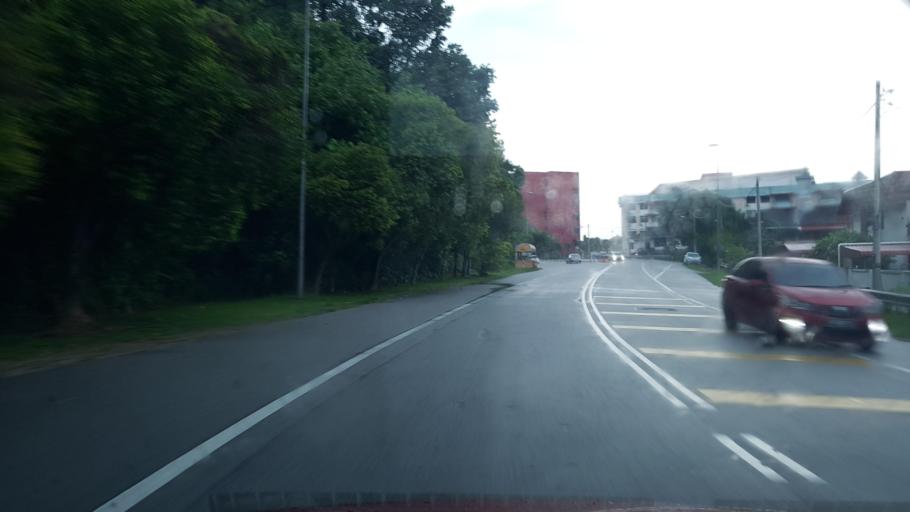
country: MY
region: Terengganu
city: Kuala Terengganu
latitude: 5.3234
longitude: 103.1382
